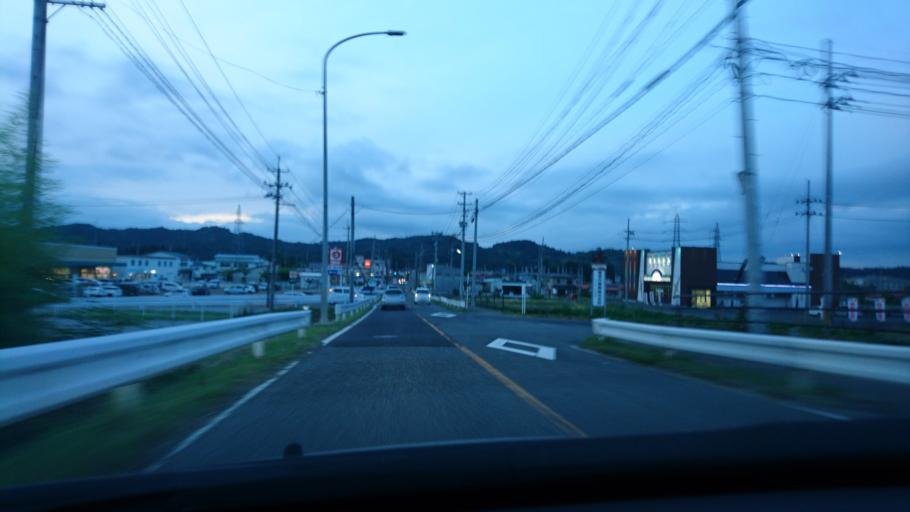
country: JP
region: Iwate
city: Ichinoseki
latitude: 38.8226
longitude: 140.9856
